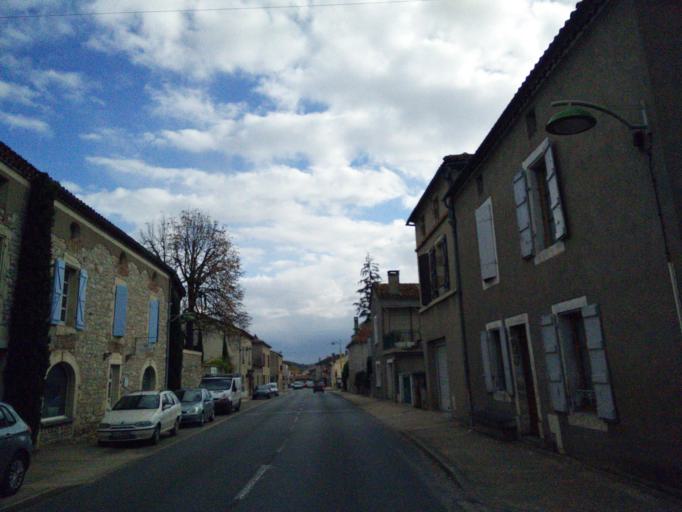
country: FR
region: Midi-Pyrenees
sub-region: Departement du Lot
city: Pradines
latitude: 44.4979
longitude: 1.3851
